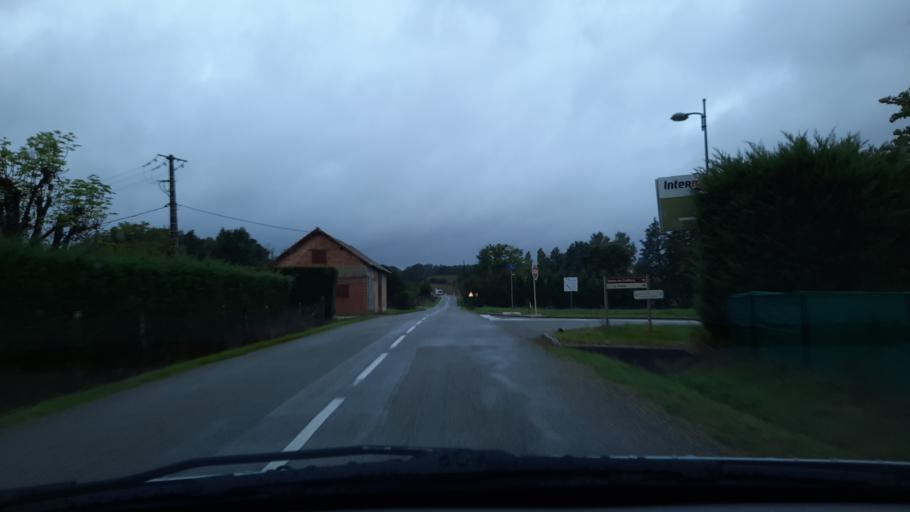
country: FR
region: Midi-Pyrenees
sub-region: Departement du Tarn-et-Garonne
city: Lafrancaise
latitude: 44.1928
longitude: 1.2849
